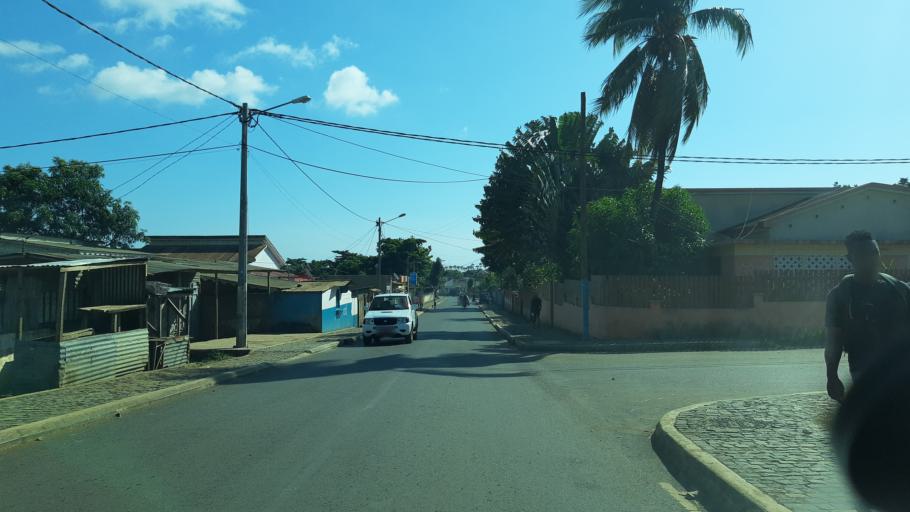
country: ST
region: Sao Tome Island
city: Sao Tome
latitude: 0.3289
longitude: 6.7296
